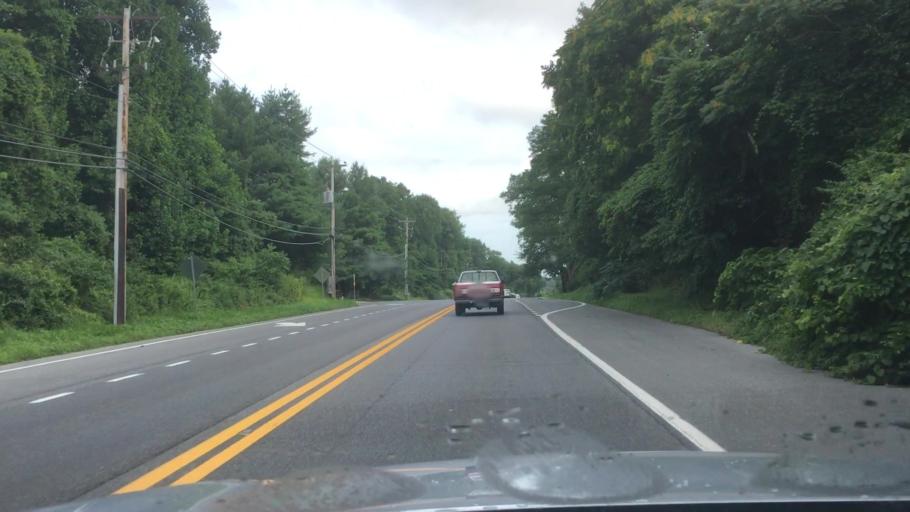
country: US
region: Delaware
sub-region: New Castle County
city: North Star
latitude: 39.7826
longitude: -75.7223
